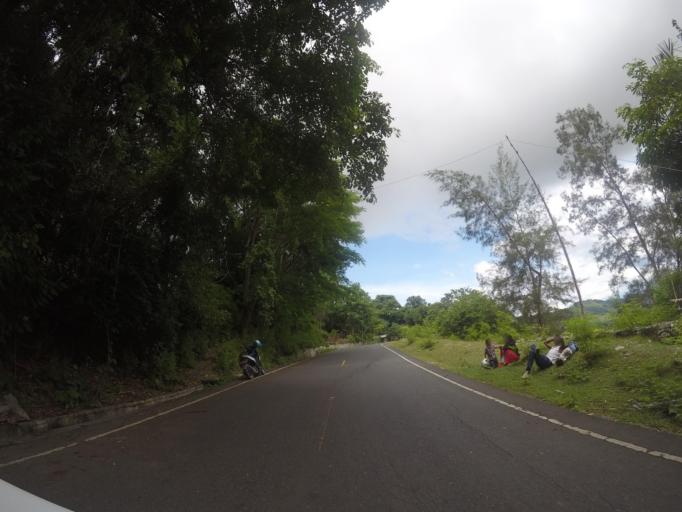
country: TL
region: Bobonaro
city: Maliana
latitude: -8.9542
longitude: 125.0745
